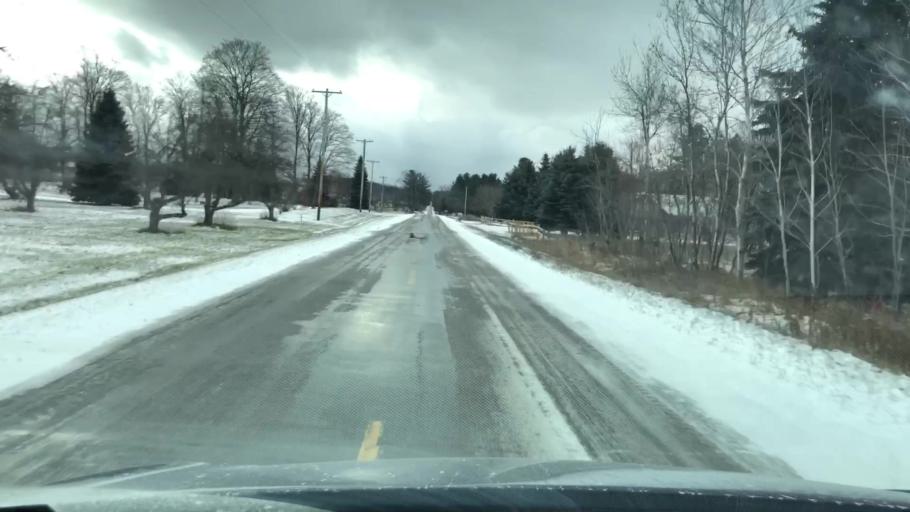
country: US
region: Michigan
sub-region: Antrim County
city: Elk Rapids
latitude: 44.9120
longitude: -85.5154
